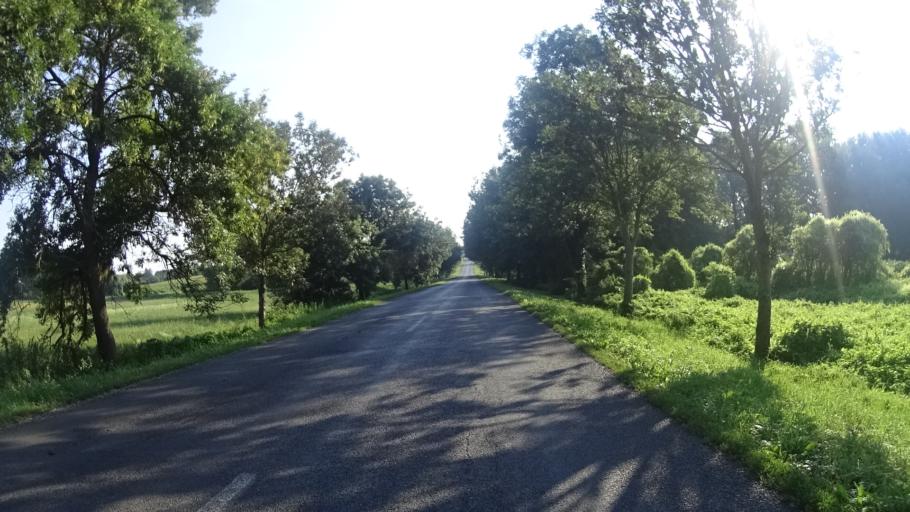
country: HU
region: Zala
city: Sarmellek
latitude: 46.6660
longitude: 17.1506
